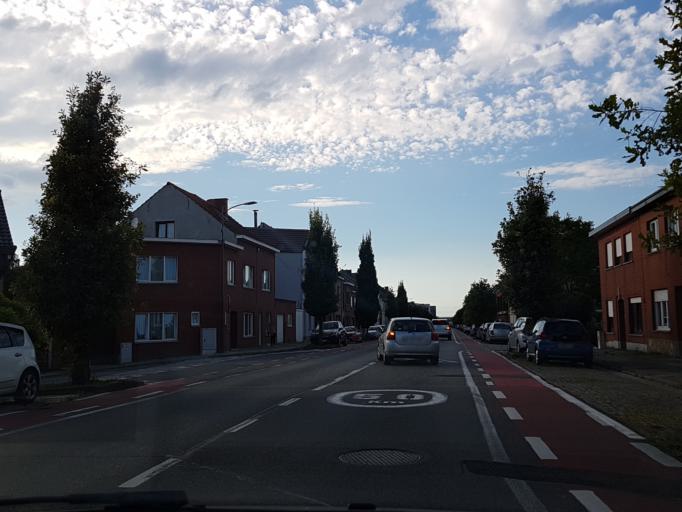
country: BE
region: Flanders
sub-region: Provincie Vlaams-Brabant
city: Herent
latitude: 50.9003
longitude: 4.6787
